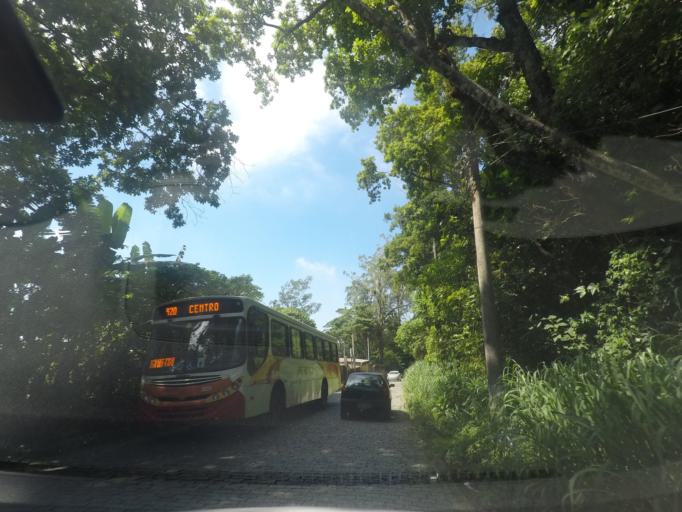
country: BR
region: Rio de Janeiro
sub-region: Petropolis
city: Petropolis
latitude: -22.5415
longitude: -43.1807
